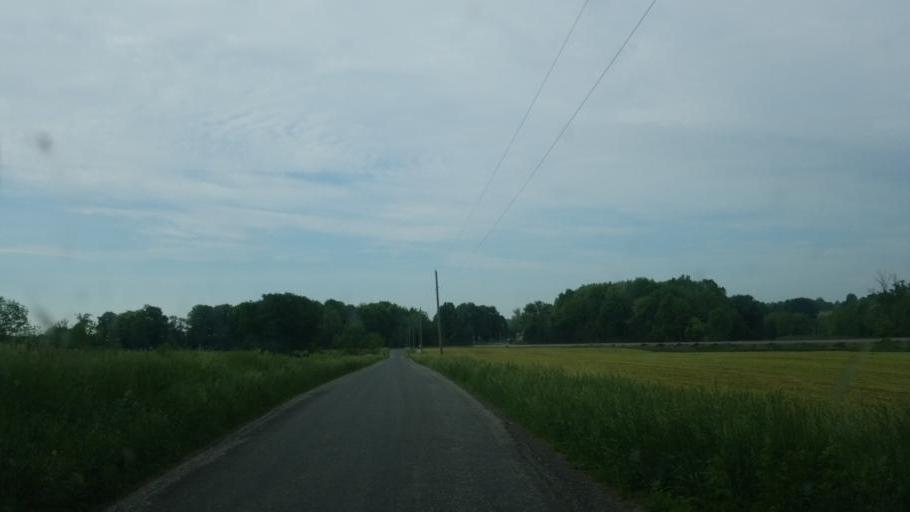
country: US
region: Ohio
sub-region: Wayne County
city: Dalton
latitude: 40.7884
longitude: -81.7259
